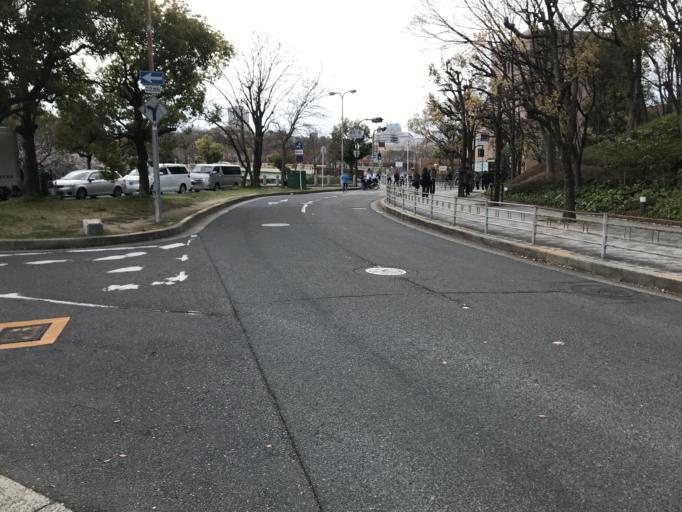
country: JP
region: Osaka
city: Osaka-shi
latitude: 34.6915
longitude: 135.5289
